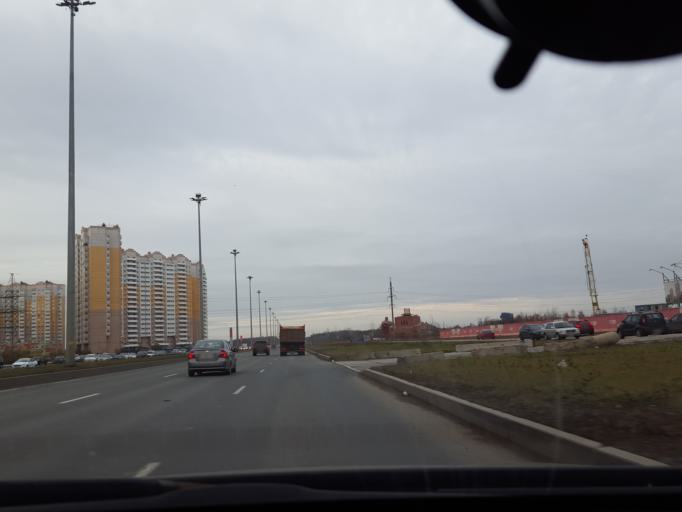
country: RU
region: St.-Petersburg
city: Kolomyagi
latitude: 60.0342
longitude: 30.2489
